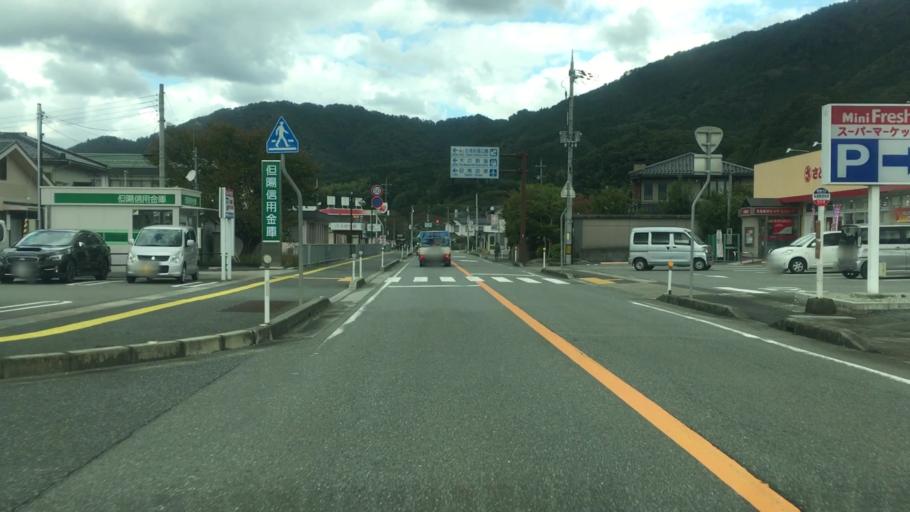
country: JP
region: Hyogo
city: Toyooka
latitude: 35.3175
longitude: 134.8829
